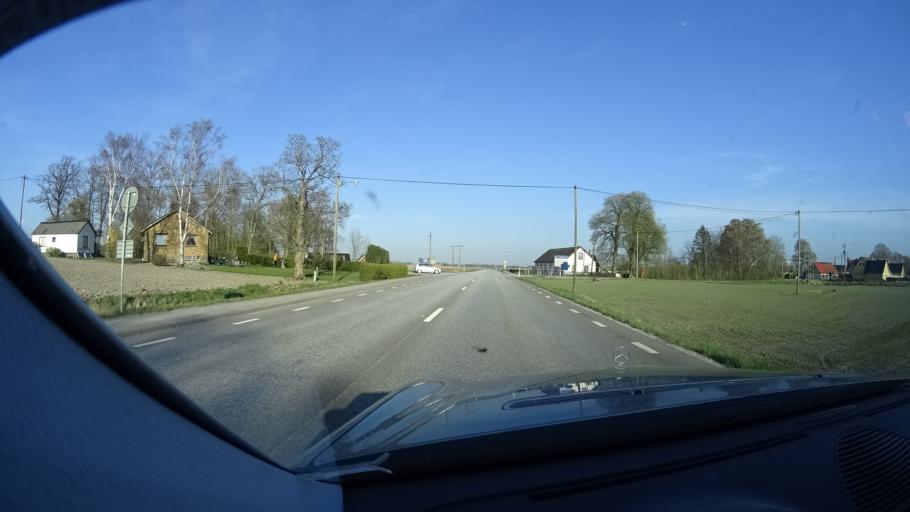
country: SE
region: Skane
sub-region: Svalovs Kommun
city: Teckomatorp
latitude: 55.8716
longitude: 13.1164
